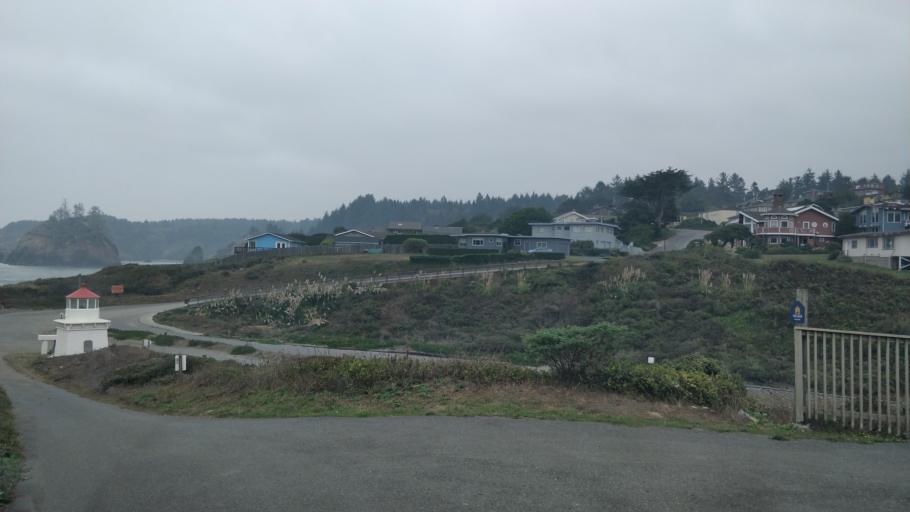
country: US
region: California
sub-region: Humboldt County
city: Westhaven-Moonstone
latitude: 41.0566
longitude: -124.1484
